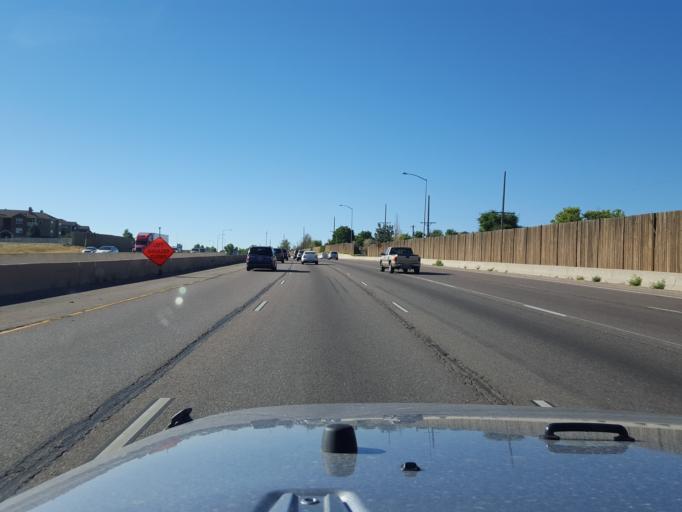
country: US
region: Colorado
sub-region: Adams County
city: Northglenn
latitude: 39.9110
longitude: -104.9908
